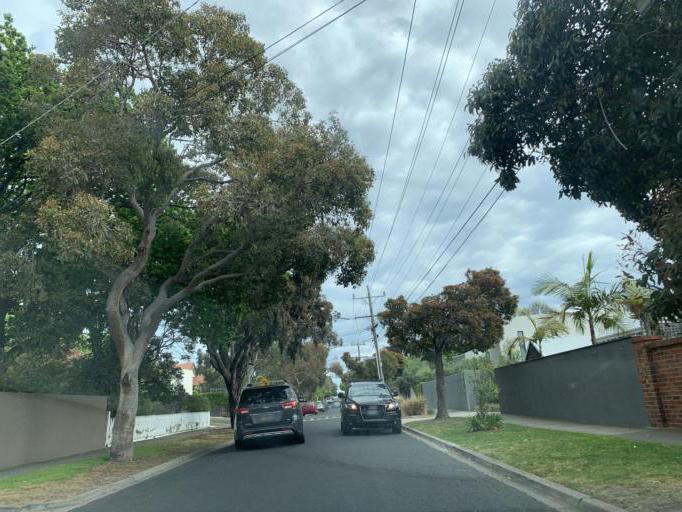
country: AU
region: Victoria
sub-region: Bayside
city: Hampton
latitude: -37.9302
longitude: 144.9997
